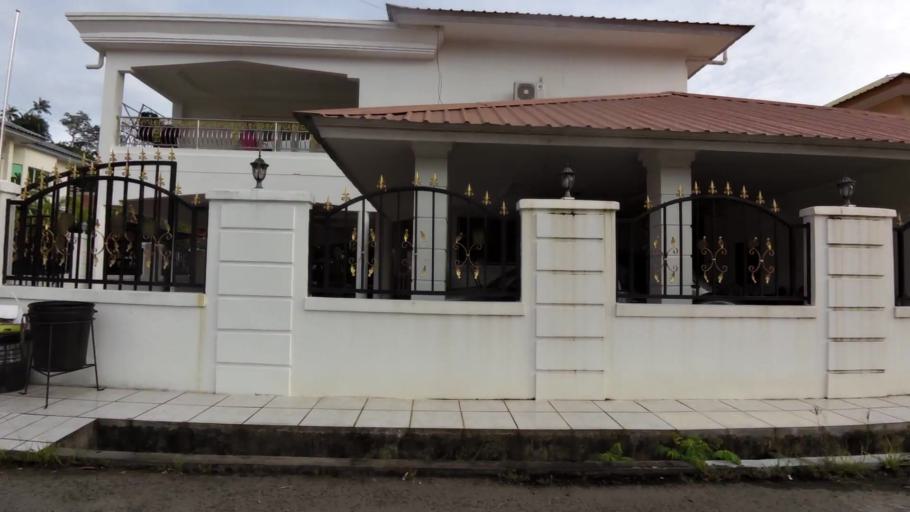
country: BN
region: Brunei and Muara
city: Bandar Seri Begawan
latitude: 4.8998
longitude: 114.8980
